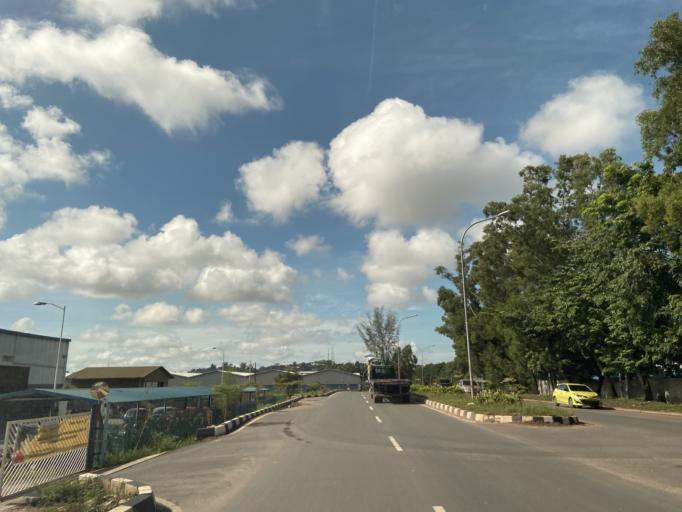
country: SG
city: Singapore
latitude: 1.1725
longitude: 104.0120
